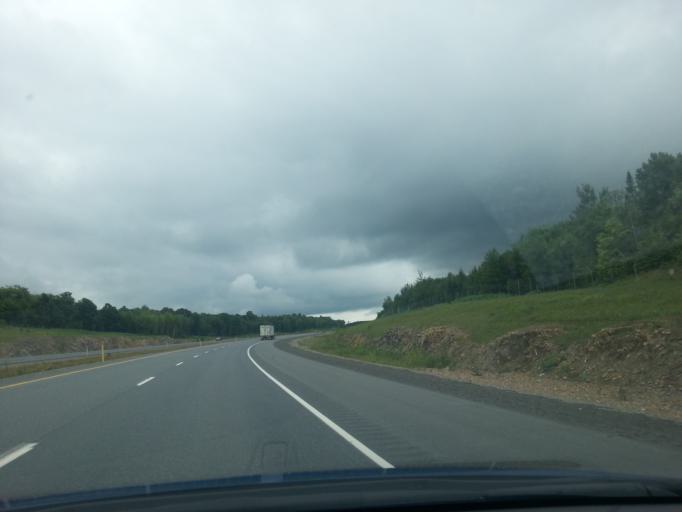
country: US
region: Maine
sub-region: Aroostook County
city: Limestone
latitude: 46.9523
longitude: -67.7386
